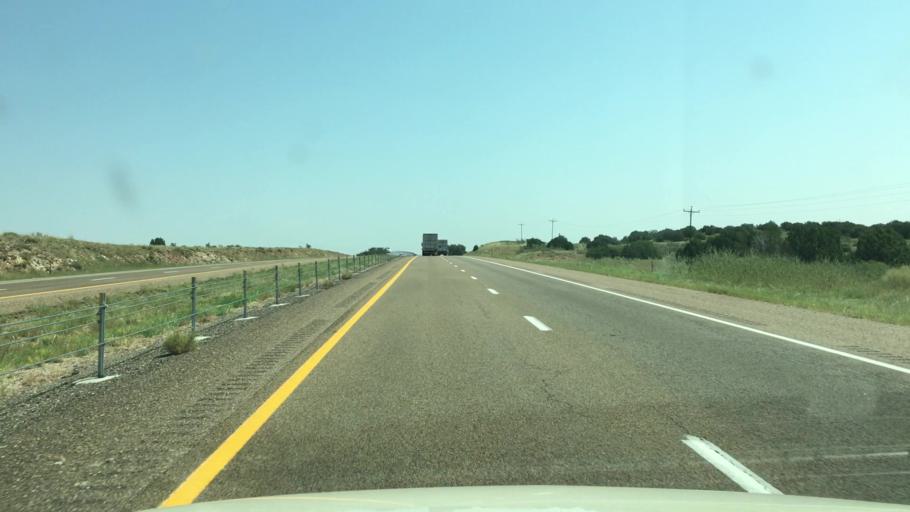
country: US
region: New Mexico
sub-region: Quay County
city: Tucumcari
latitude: 35.1233
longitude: -103.8562
